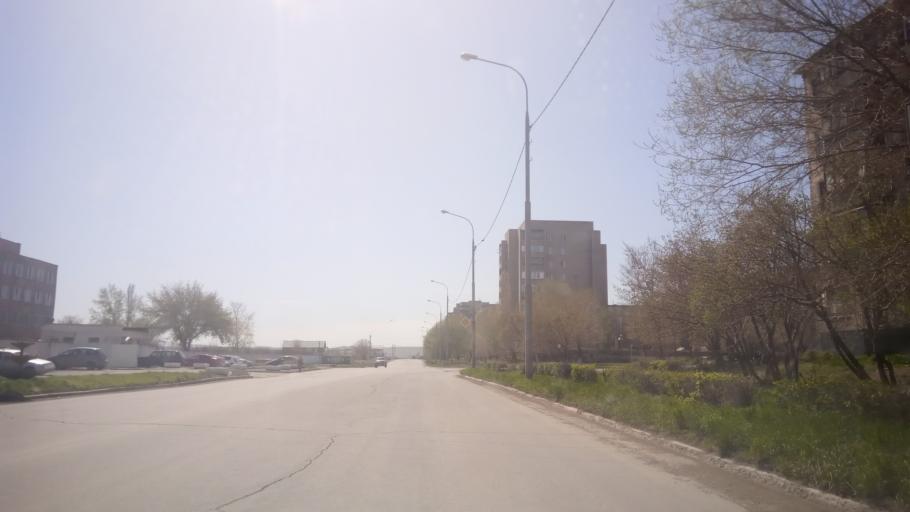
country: RU
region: Orenburg
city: Novotroitsk
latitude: 51.1839
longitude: 58.2850
